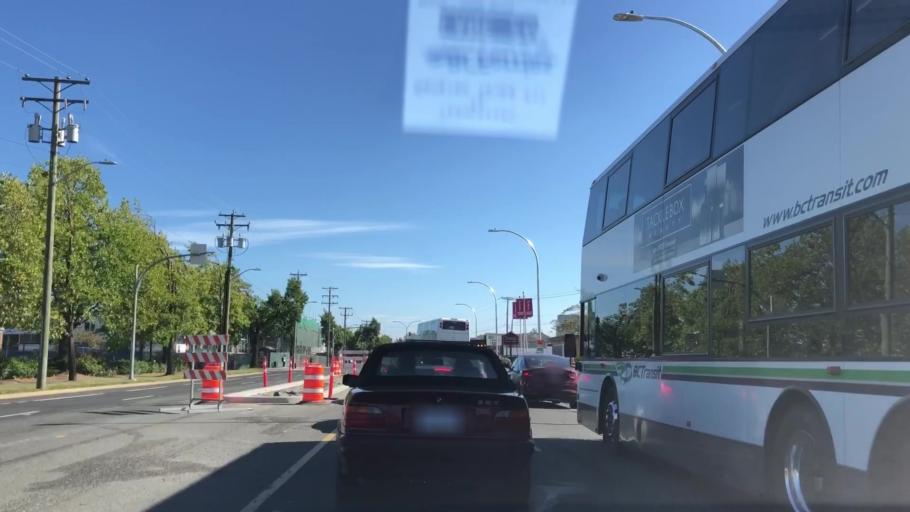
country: CA
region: British Columbia
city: Victoria
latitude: 48.4434
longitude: -123.3698
